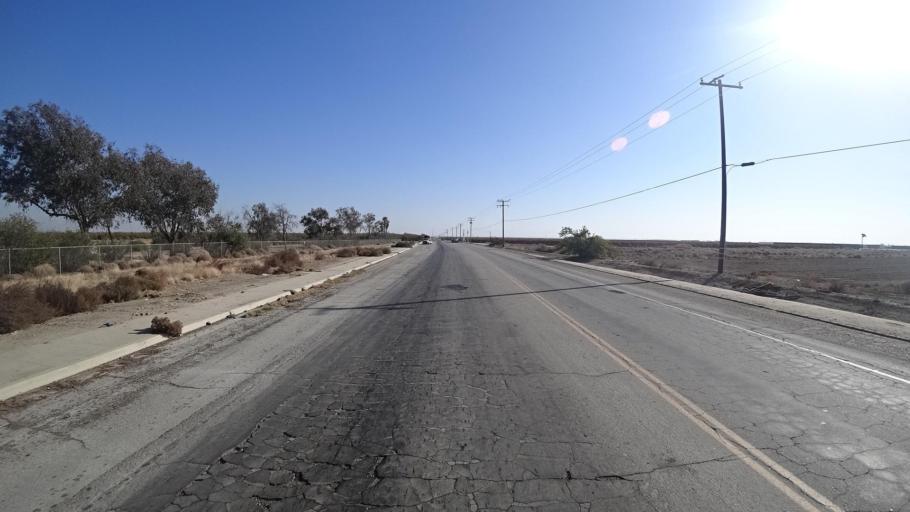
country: US
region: California
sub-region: Kern County
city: McFarland
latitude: 35.7180
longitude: -119.2323
